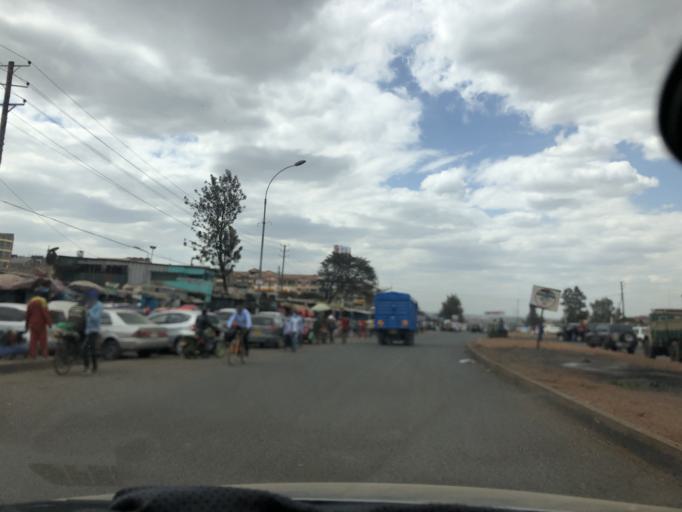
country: KE
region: Nairobi Area
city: Pumwani
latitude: -1.2189
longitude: 36.8905
